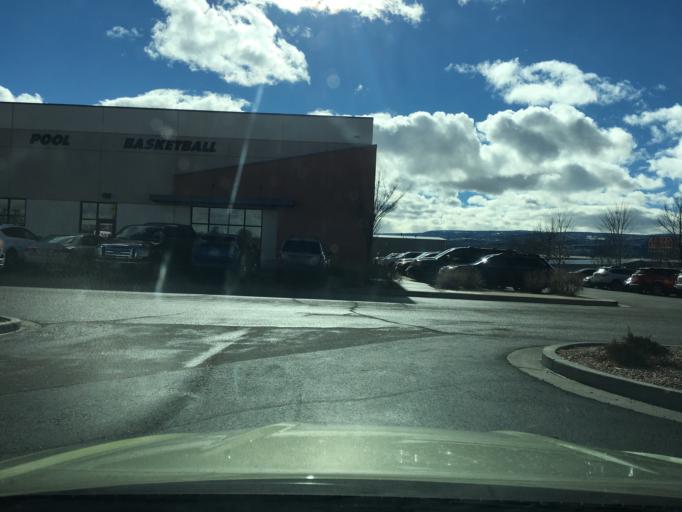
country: US
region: Colorado
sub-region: Mesa County
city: Grand Junction
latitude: 39.0748
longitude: -108.5767
